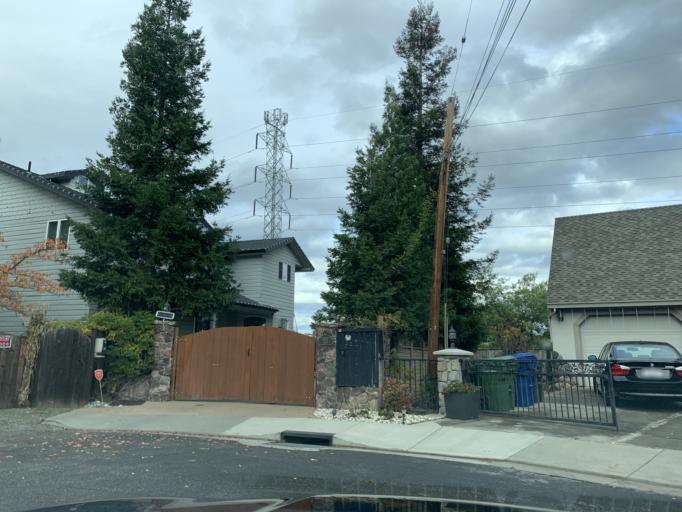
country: US
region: California
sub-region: Santa Clara County
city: Monte Sereno
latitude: 37.2607
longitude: -121.9732
